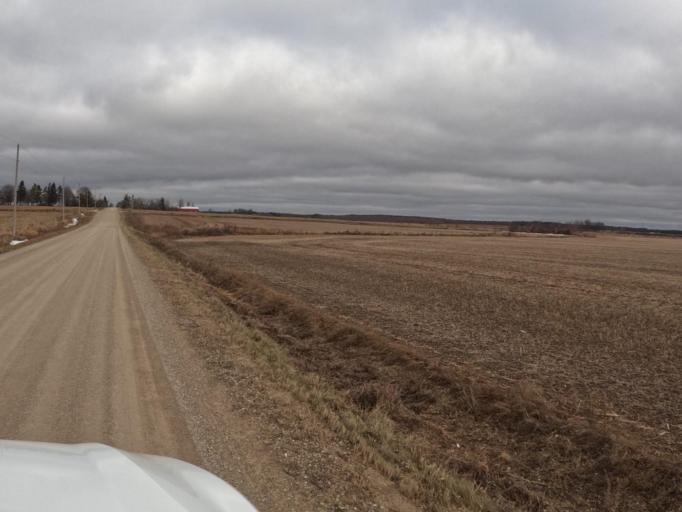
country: CA
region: Ontario
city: Shelburne
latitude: 44.0045
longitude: -80.4104
